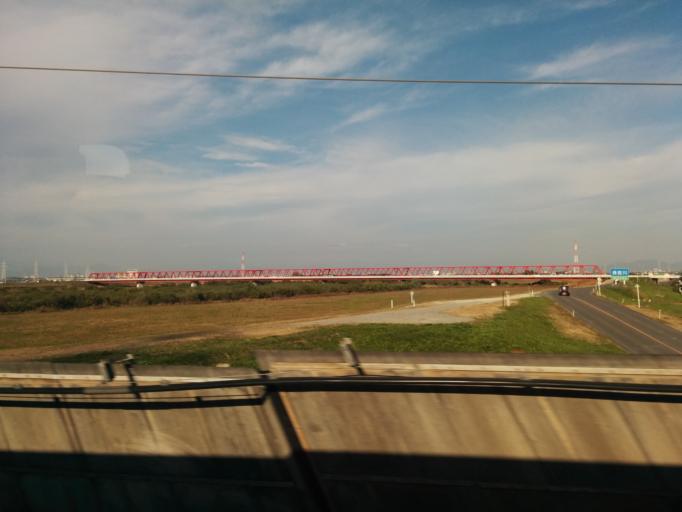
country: JP
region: Gifu
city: Ogaki
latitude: 35.3398
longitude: 136.6524
